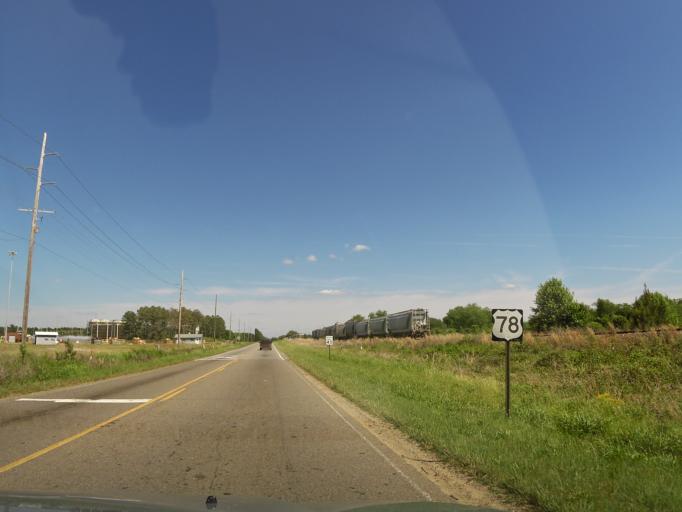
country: US
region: South Carolina
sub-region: Aiken County
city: Aiken
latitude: 33.5432
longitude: -81.6722
